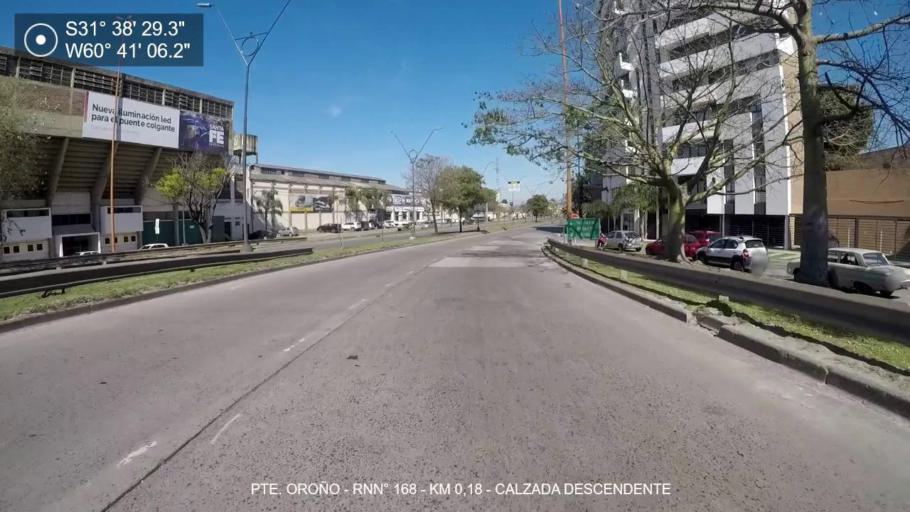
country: AR
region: Santa Fe
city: Santa Fe de la Vera Cruz
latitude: -31.6414
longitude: -60.6850
